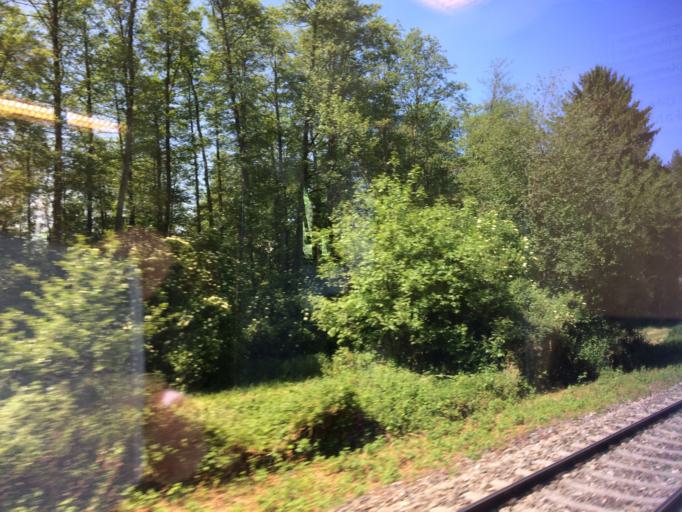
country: DE
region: Baden-Wuerttemberg
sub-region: Tuebingen Region
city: Meckenbeuren
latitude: 47.6885
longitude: 9.5532
